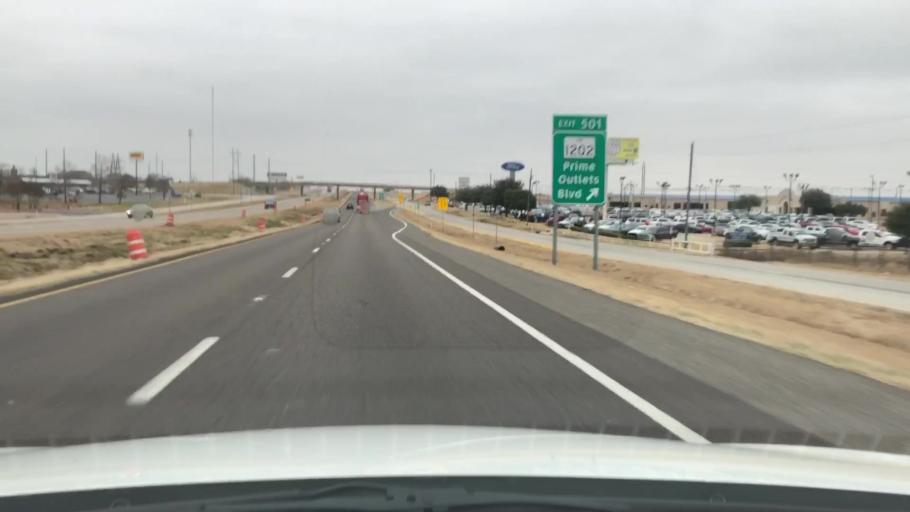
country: US
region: Texas
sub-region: Cooke County
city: Gainesville
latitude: 33.6780
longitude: -97.1541
